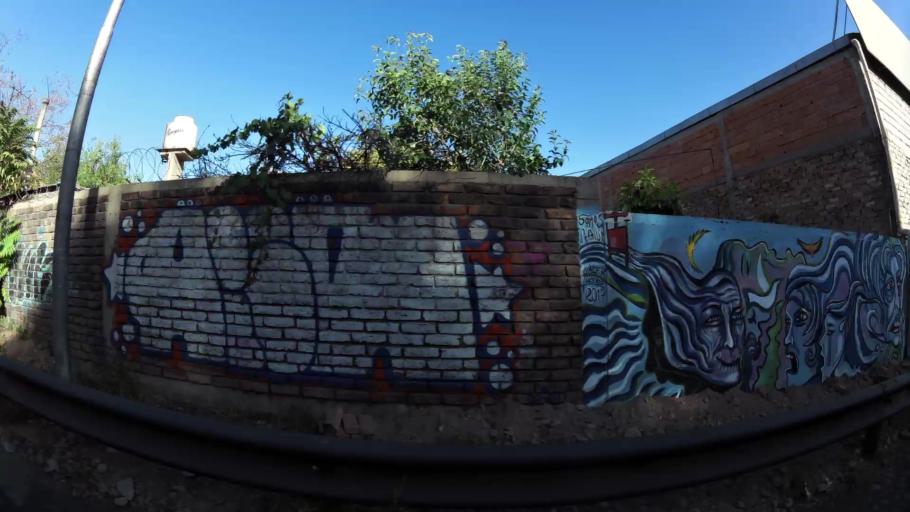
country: AR
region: Mendoza
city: Mendoza
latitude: -32.9050
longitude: -68.8381
